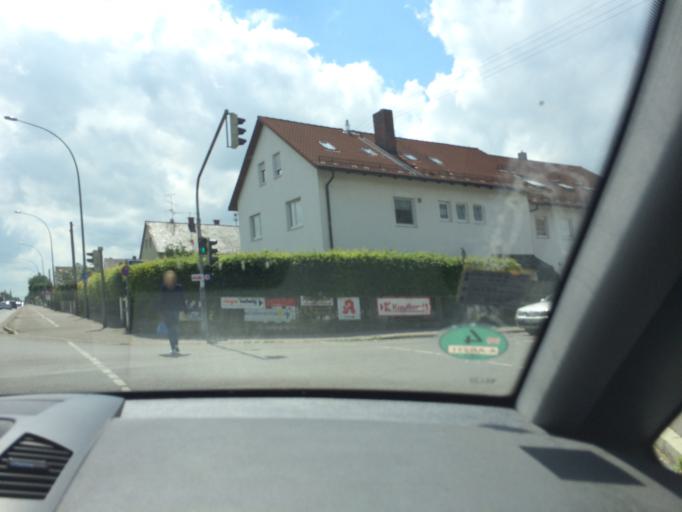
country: DE
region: Bavaria
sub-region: Swabia
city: Konigsbrunn
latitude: 48.2892
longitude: 10.8965
